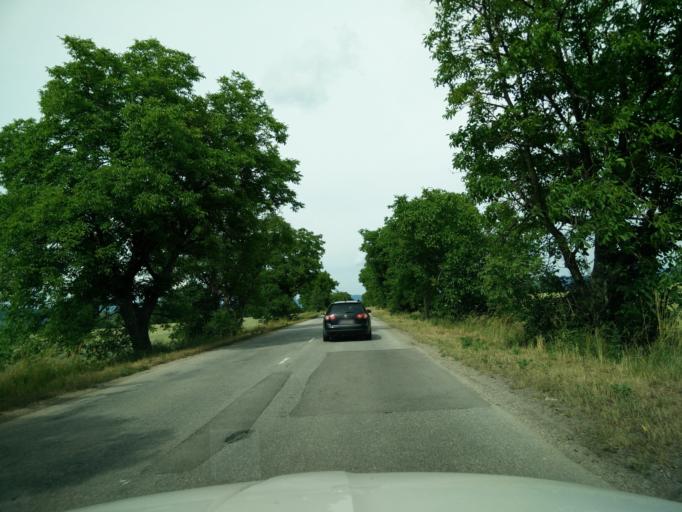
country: SK
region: Nitriansky
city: Novaky
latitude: 48.7339
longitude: 18.5675
